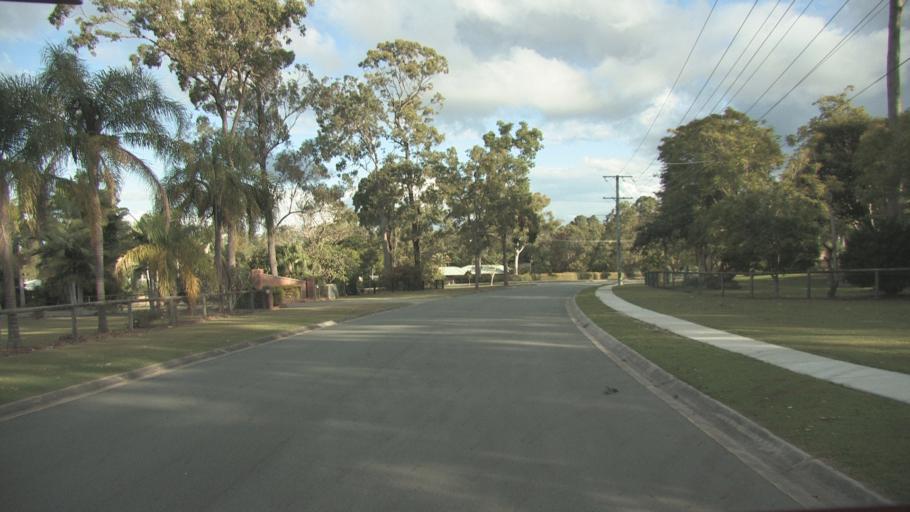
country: AU
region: Queensland
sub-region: Logan
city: Park Ridge South
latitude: -27.7008
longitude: 153.0160
